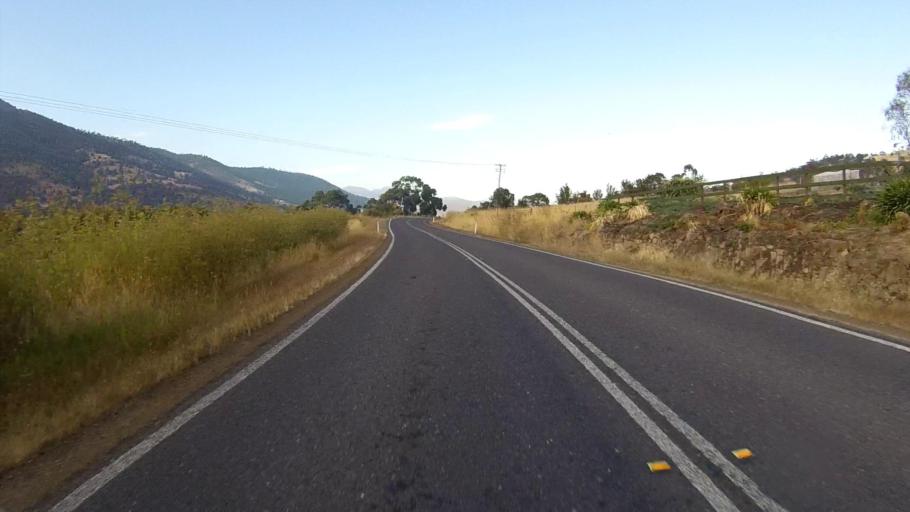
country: AU
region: Tasmania
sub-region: Glenorchy
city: Granton
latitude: -42.7496
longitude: 147.1528
